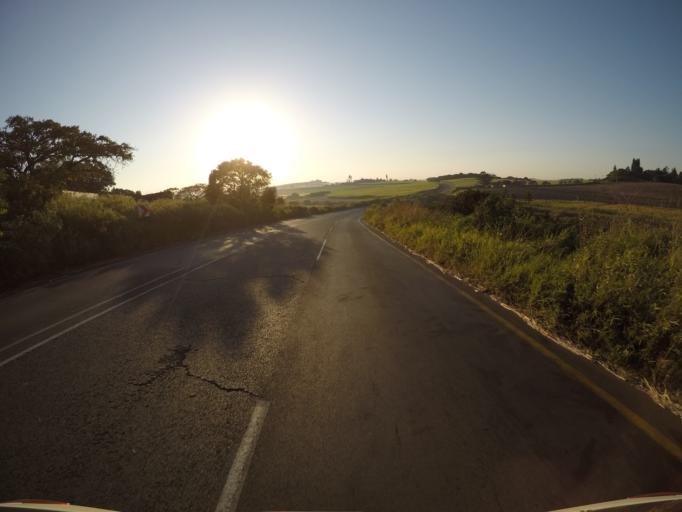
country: ZA
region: KwaZulu-Natal
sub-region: uThungulu District Municipality
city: eSikhawini
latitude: -28.9491
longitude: 31.6907
